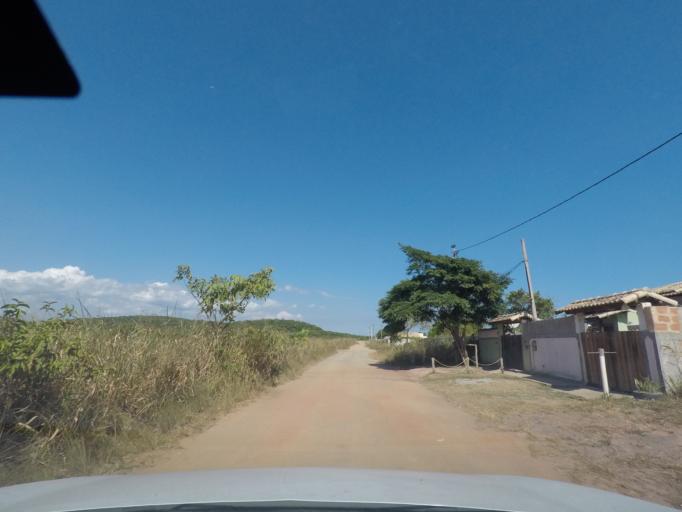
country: BR
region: Rio de Janeiro
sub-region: Marica
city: Marica
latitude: -22.9645
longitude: -42.9072
